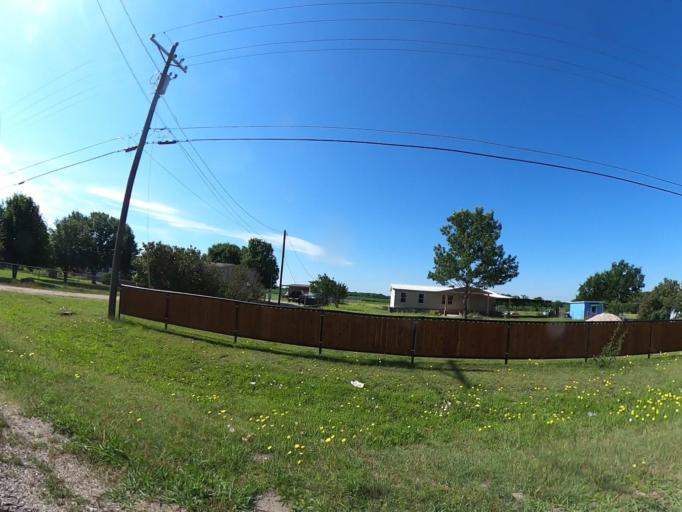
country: US
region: Texas
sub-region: Ellis County
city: Red Oak
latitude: 32.4419
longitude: -96.7783
